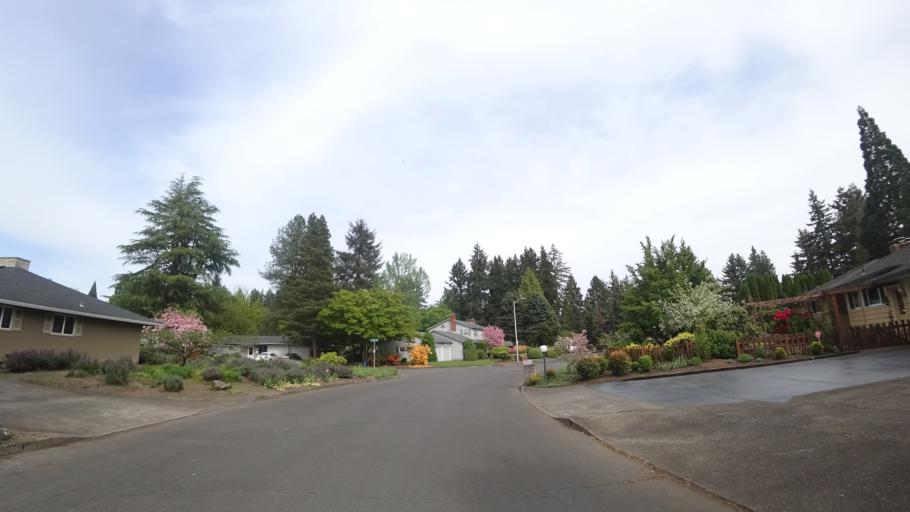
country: US
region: Oregon
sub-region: Washington County
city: Hillsboro
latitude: 45.5088
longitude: -122.9462
